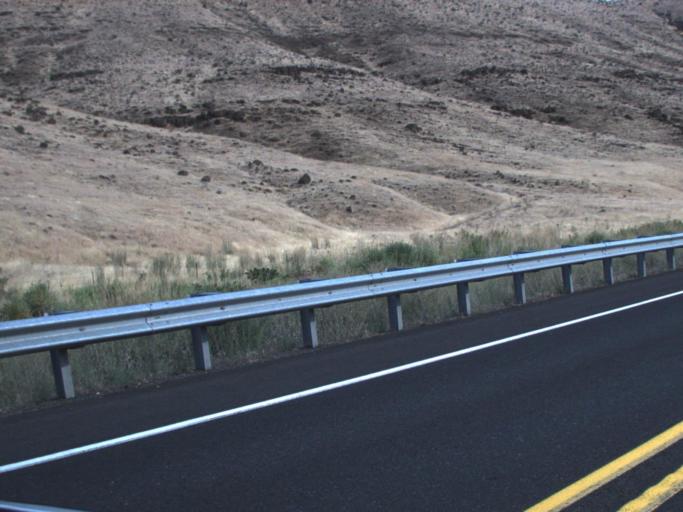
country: US
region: Washington
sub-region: Yakima County
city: Toppenish
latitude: 46.1968
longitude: -120.4880
